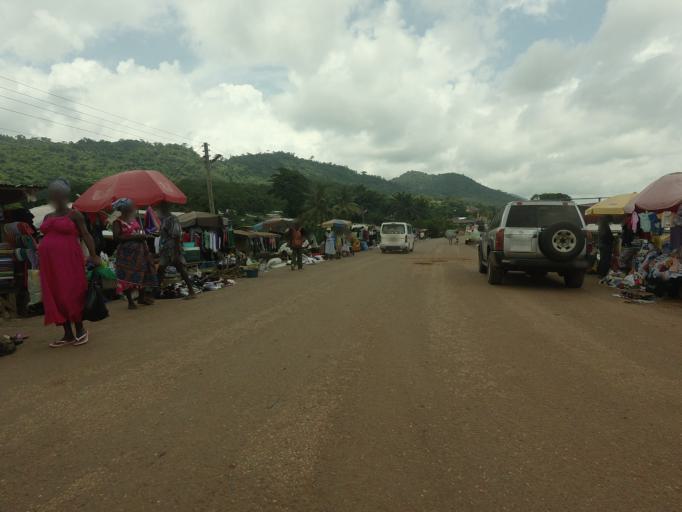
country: GH
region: Volta
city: Ho
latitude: 6.6840
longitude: 0.3327
